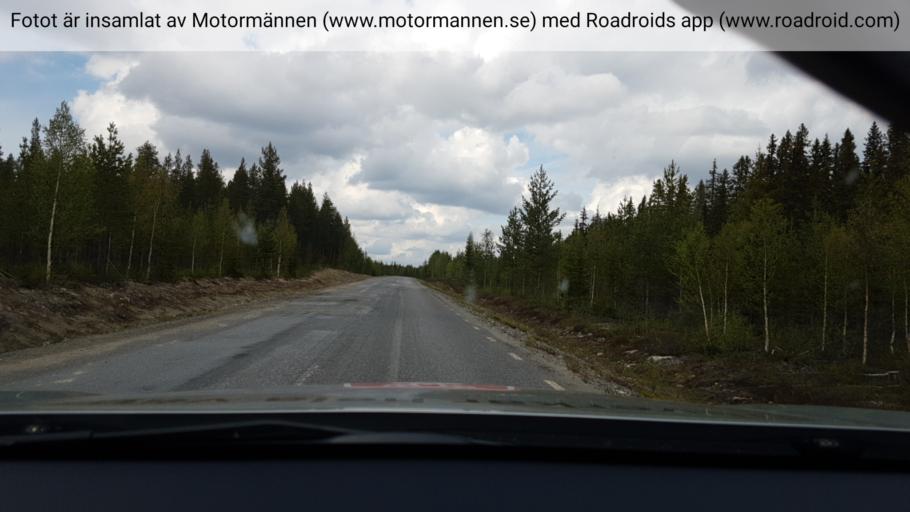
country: SE
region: Vaesterbotten
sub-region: Lycksele Kommun
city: Lycksele
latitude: 63.9741
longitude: 18.4956
